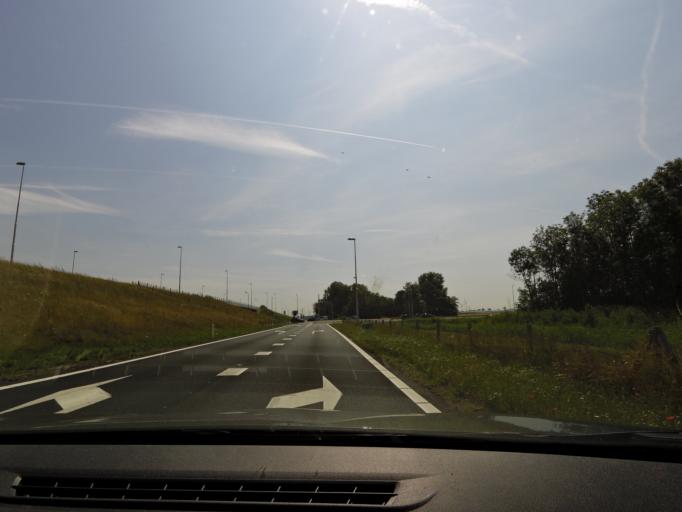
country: NL
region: South Holland
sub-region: Gemeente Brielle
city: Brielle
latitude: 51.8915
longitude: 4.1970
